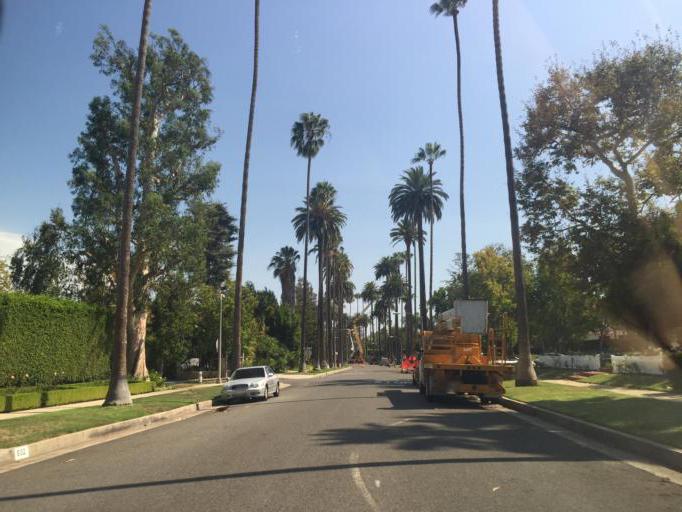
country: US
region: California
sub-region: Los Angeles County
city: Beverly Hills
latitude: 34.0784
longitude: -118.4008
